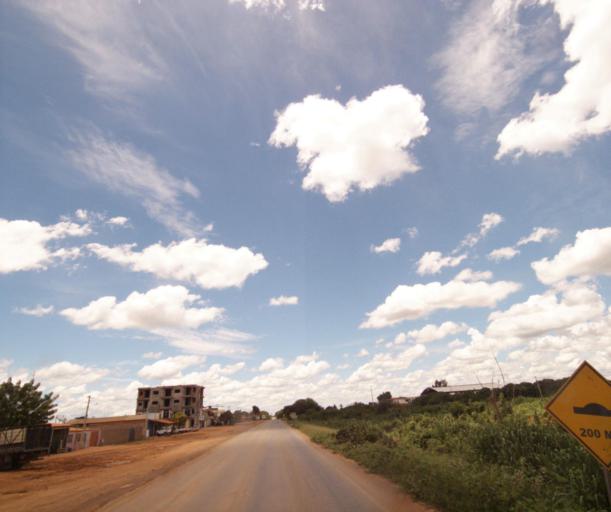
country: BR
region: Bahia
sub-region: Bom Jesus Da Lapa
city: Bom Jesus da Lapa
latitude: -13.2659
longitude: -43.5972
